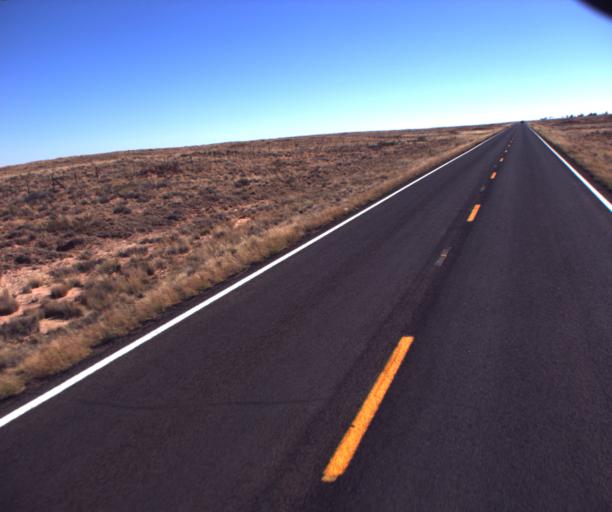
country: US
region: Arizona
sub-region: Coconino County
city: Tuba City
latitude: 35.9675
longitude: -110.9554
